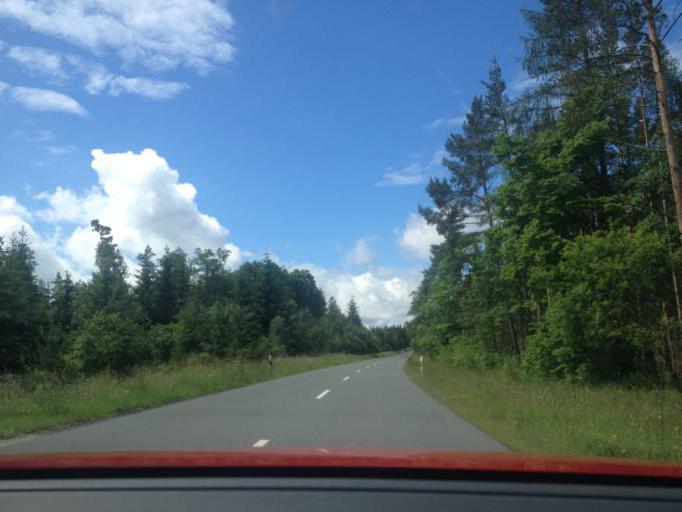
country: DE
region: Bavaria
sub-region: Upper Palatinate
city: Pechbrunn
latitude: 49.9921
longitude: 12.1855
